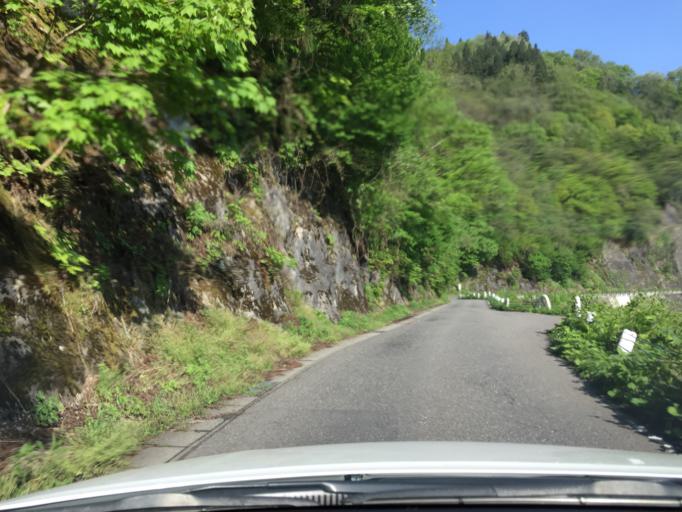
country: JP
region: Fukushima
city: Kitakata
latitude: 37.6647
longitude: 139.5920
